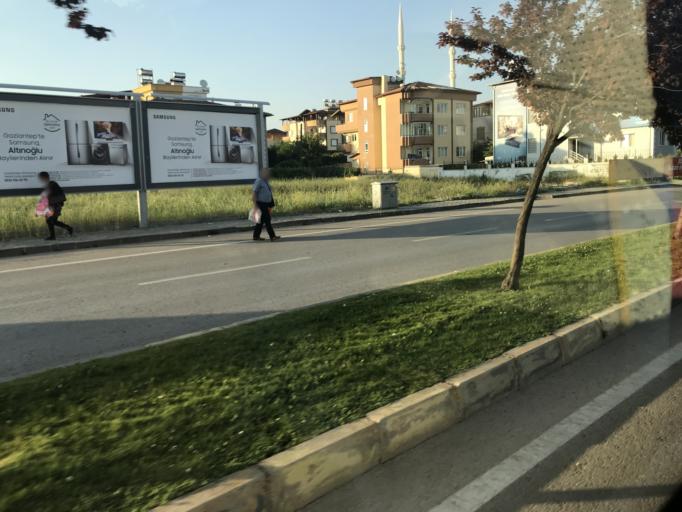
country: TR
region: Gaziantep
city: Sahinbey
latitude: 37.0564
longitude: 37.3285
